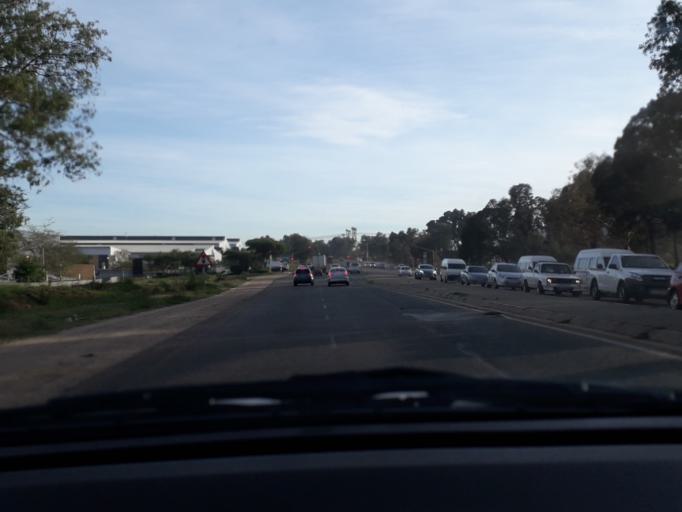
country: ZA
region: Gauteng
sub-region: City of Johannesburg Metropolitan Municipality
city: Midrand
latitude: -25.9270
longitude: 28.1503
